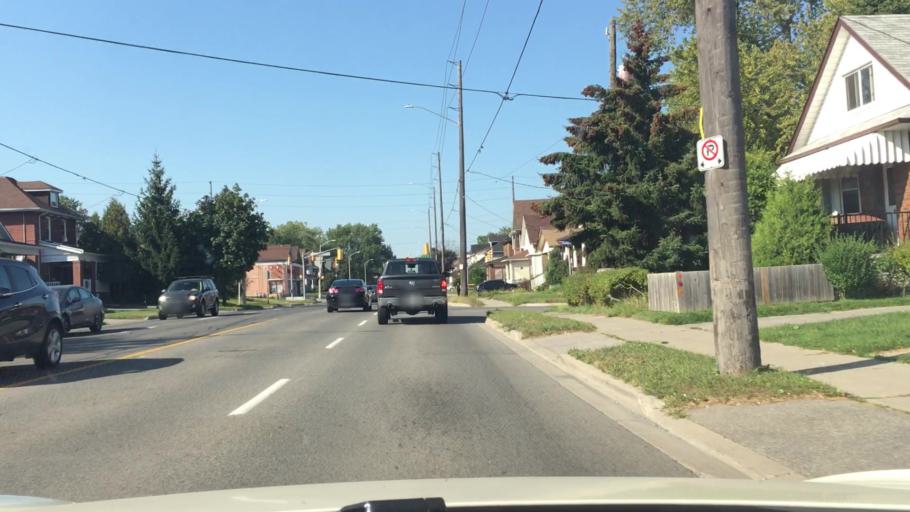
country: CA
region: Ontario
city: Oshawa
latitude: 43.8941
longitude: -78.8511
